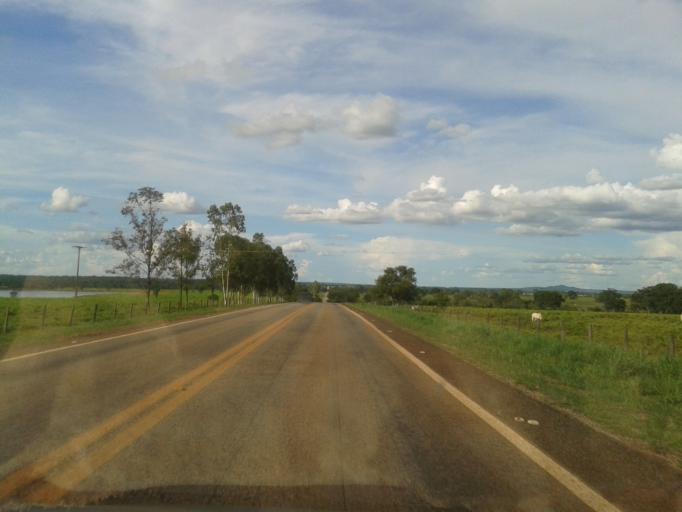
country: BR
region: Goias
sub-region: Crixas
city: Crixas
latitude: -14.2469
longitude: -50.3963
